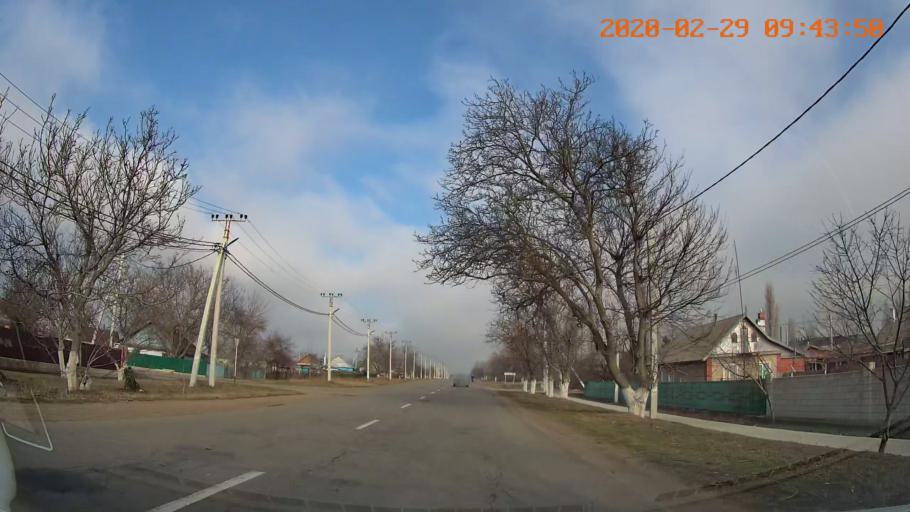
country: MD
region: Telenesti
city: Crasnoe
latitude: 46.6475
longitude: 29.8197
